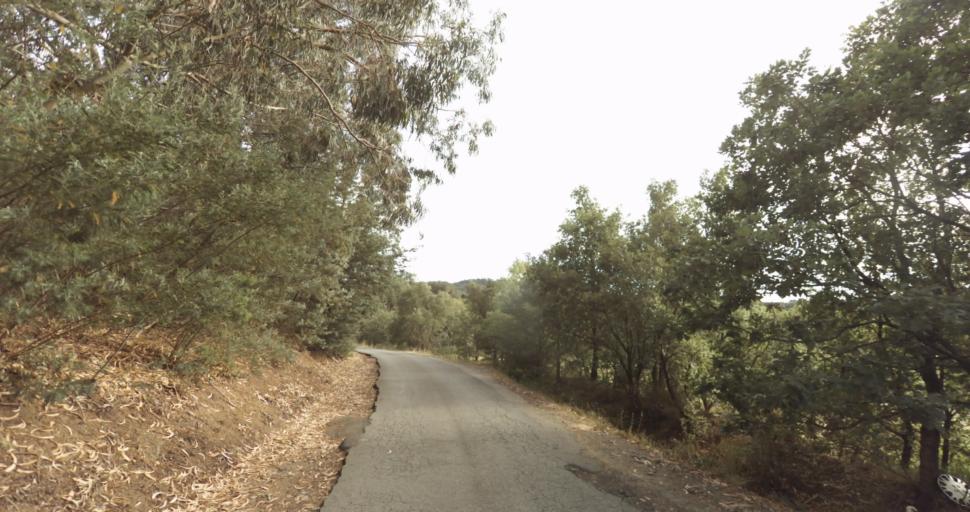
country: FR
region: Provence-Alpes-Cote d'Azur
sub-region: Departement du Var
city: Gassin
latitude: 43.2206
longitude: 6.5808
